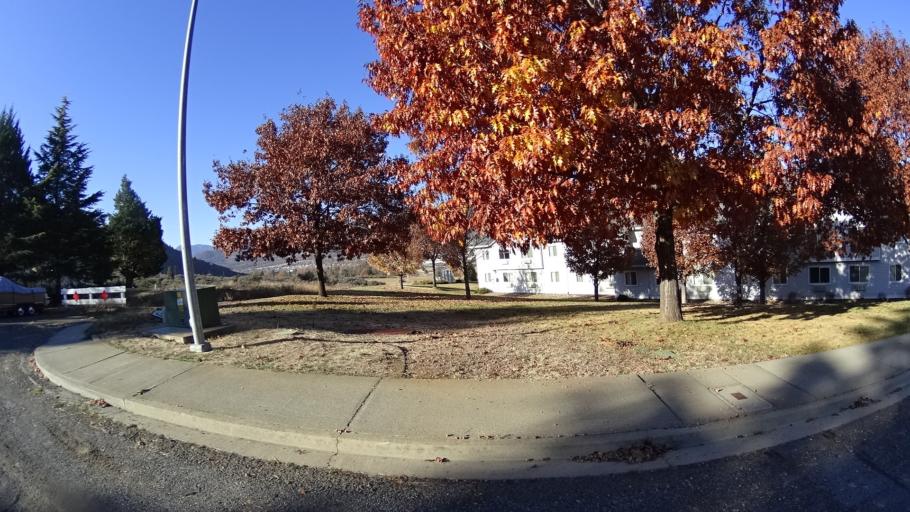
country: US
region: California
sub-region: Siskiyou County
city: Yreka
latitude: 41.7327
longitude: -122.6242
